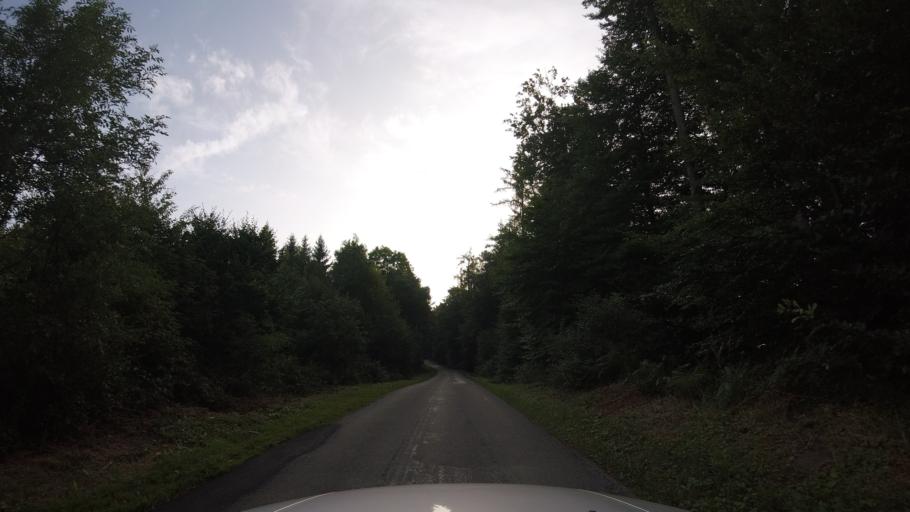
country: DE
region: Baden-Wuerttemberg
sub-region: Regierungsbezirk Stuttgart
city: Aspach
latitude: 49.0096
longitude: 9.3921
